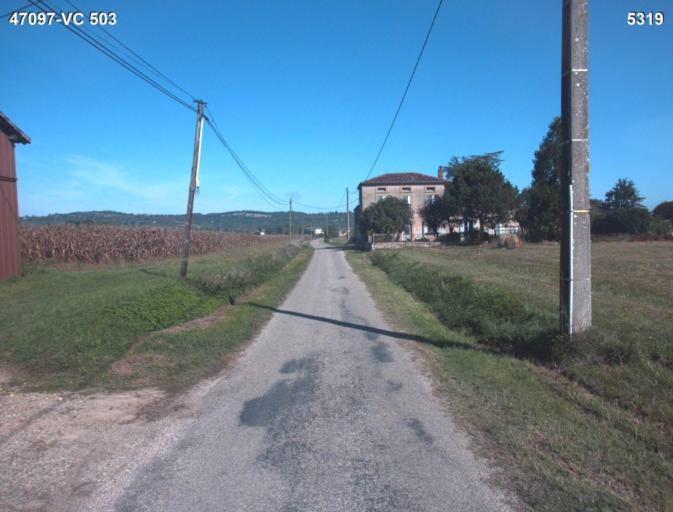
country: FR
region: Aquitaine
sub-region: Departement du Lot-et-Garonne
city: Port-Sainte-Marie
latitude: 44.2314
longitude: 0.3866
